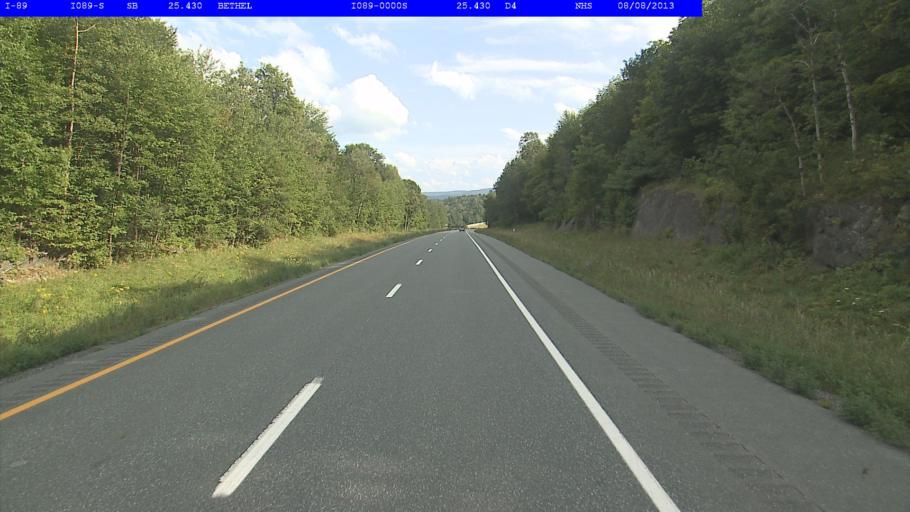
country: US
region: Vermont
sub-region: Orange County
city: Randolph
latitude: 43.8681
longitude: -72.6105
